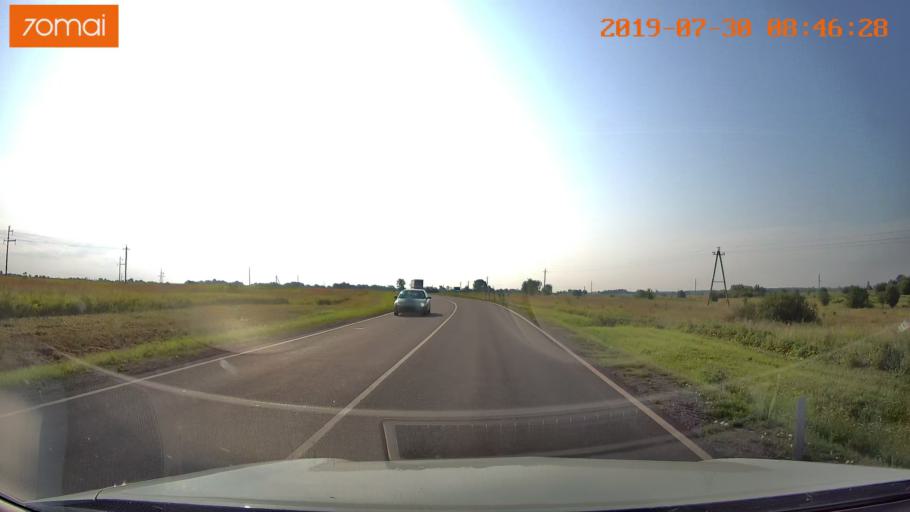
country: RU
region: Kaliningrad
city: Chernyakhovsk
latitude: 54.6231
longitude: 21.8845
